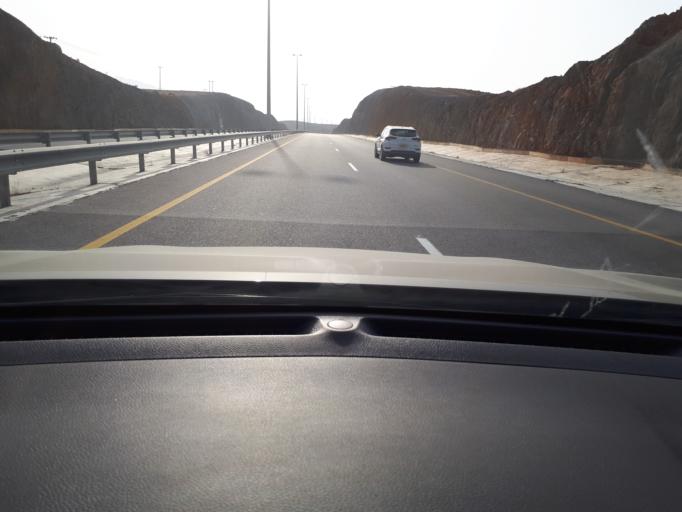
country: OM
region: Muhafazat Masqat
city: Muscat
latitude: 23.1907
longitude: 58.8487
